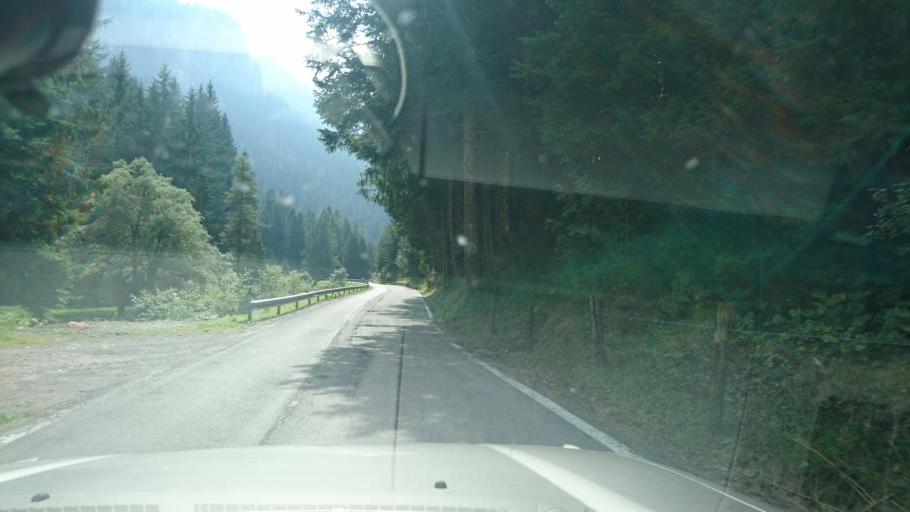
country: IT
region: Lombardy
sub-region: Provincia di Brescia
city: Bagolino
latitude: 45.8992
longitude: 10.4616
